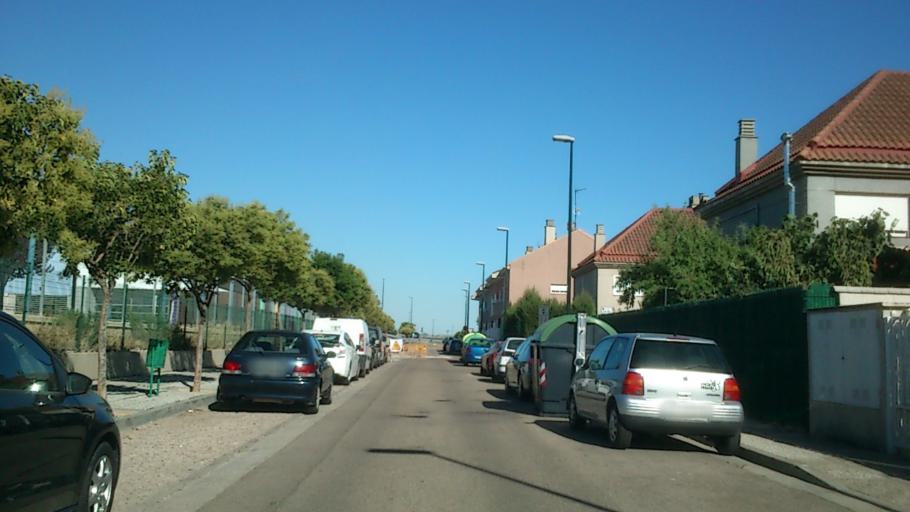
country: ES
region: Aragon
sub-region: Provincia de Zaragoza
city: Zaragoza
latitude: 41.6690
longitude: -0.8217
